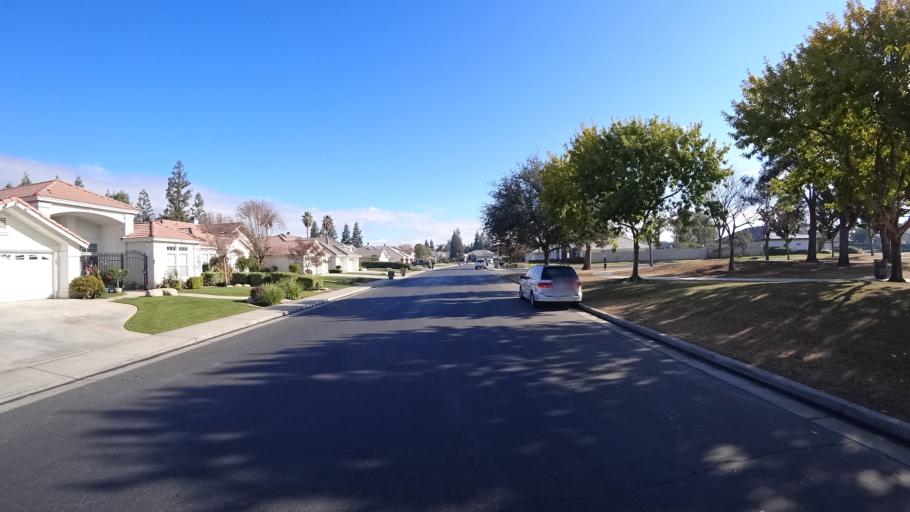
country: US
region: California
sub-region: Kern County
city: Greenacres
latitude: 35.3448
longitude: -119.1217
